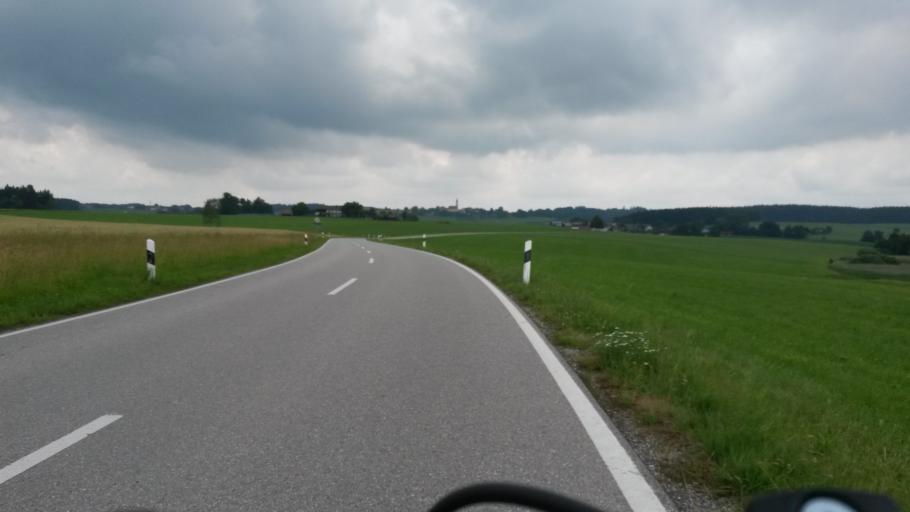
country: DE
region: Bavaria
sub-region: Upper Bavaria
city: Hoslwang
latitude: 47.9356
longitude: 12.3436
